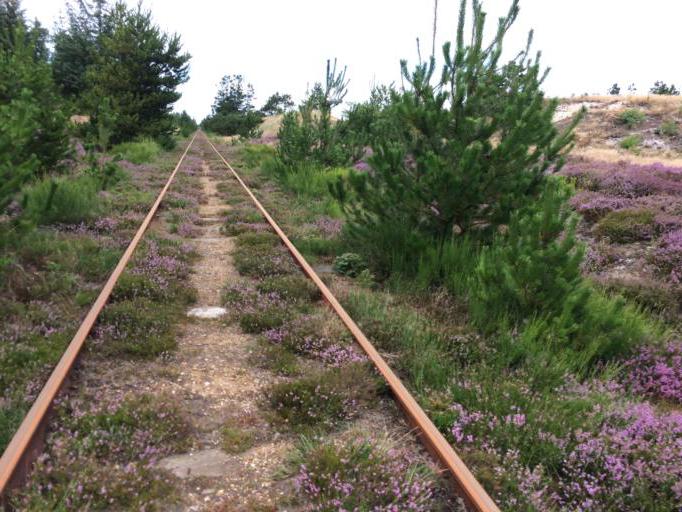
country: DK
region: South Denmark
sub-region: Varde Kommune
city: Oksbol
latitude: 55.7995
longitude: 8.2223
